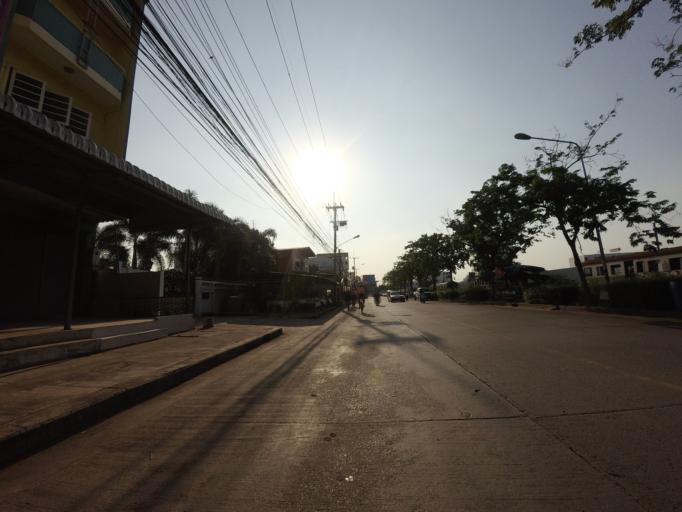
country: TH
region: Samut Sakhon
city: Samut Sakhon
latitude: 13.5488
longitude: 100.2830
